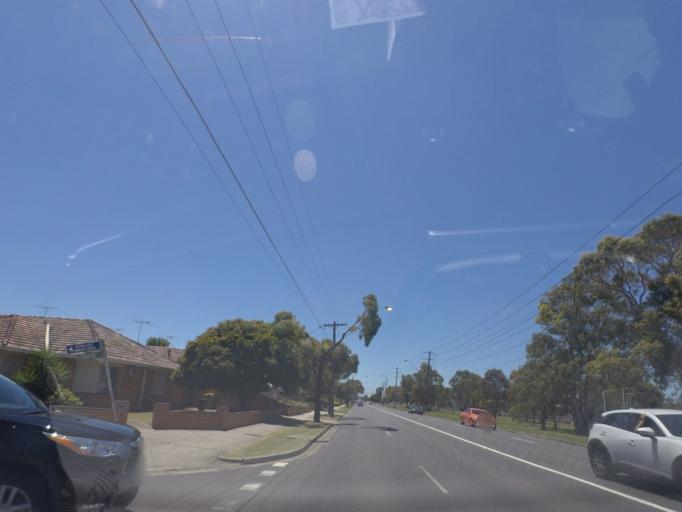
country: AU
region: Victoria
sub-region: Whittlesea
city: Thomastown
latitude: -37.6987
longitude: 145.0107
